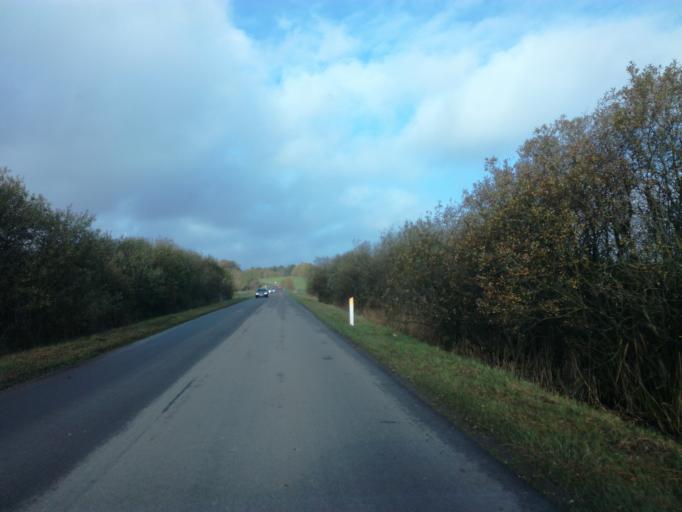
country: DK
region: South Denmark
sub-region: Fredericia Kommune
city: Fredericia
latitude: 55.6218
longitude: 9.7385
